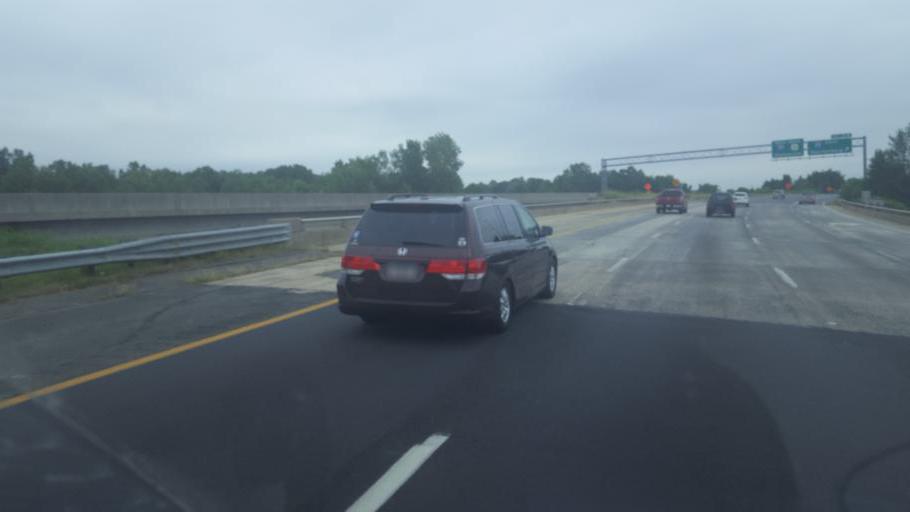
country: US
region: North Carolina
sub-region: Mecklenburg County
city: Charlotte
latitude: 35.2721
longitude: -80.8468
